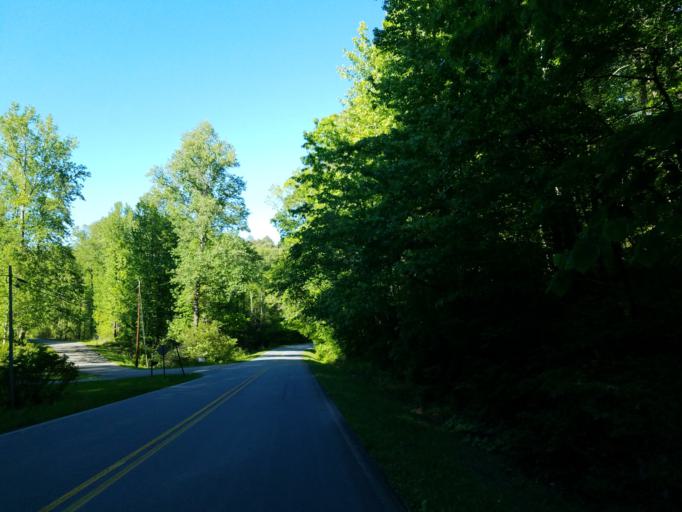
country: US
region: Georgia
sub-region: Pickens County
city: Jasper
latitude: 34.5659
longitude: -84.5172
